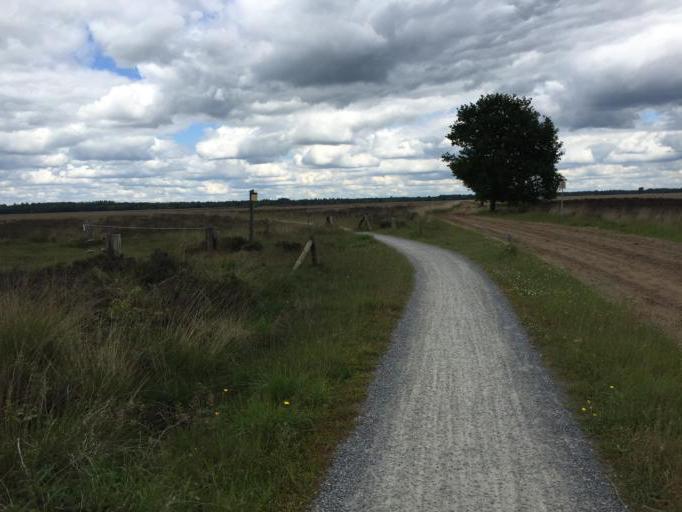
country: NL
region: Drenthe
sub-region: Gemeente Westerveld
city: Dwingeloo
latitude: 52.7964
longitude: 6.3963
